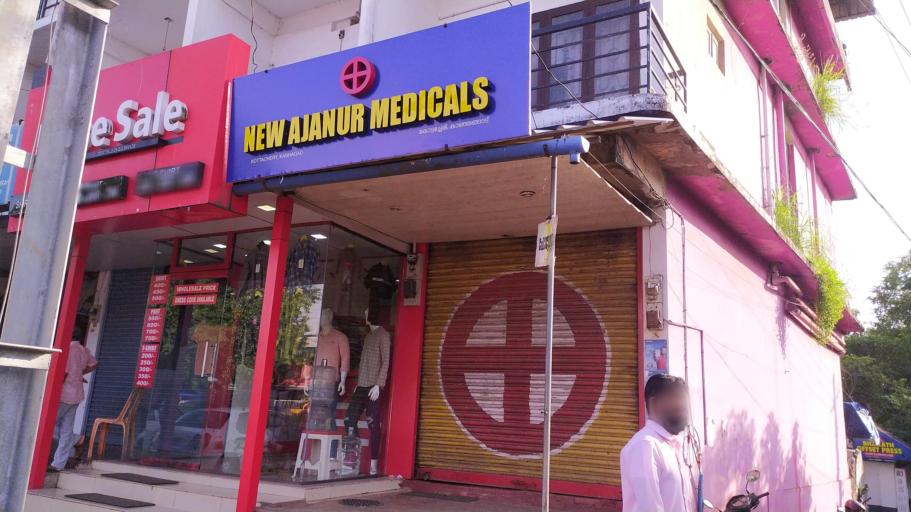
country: IN
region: Kerala
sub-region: Kasaragod District
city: Kannangad
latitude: 12.3252
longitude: 75.0848
